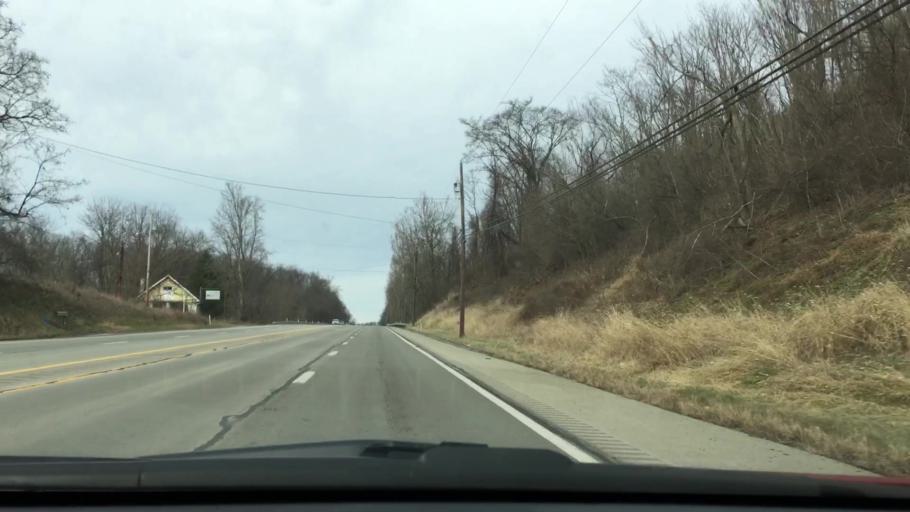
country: US
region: Pennsylvania
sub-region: Fayette County
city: Perryopolis
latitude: 40.1005
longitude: -79.7654
